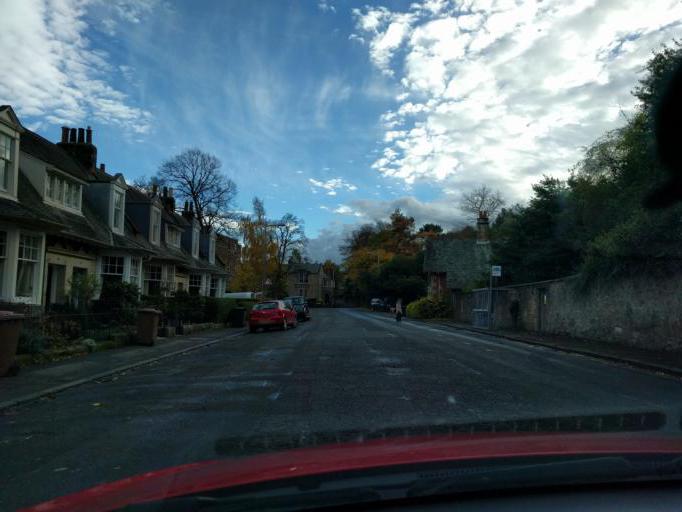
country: GB
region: Scotland
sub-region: Edinburgh
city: Colinton
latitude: 55.9230
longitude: -3.2239
